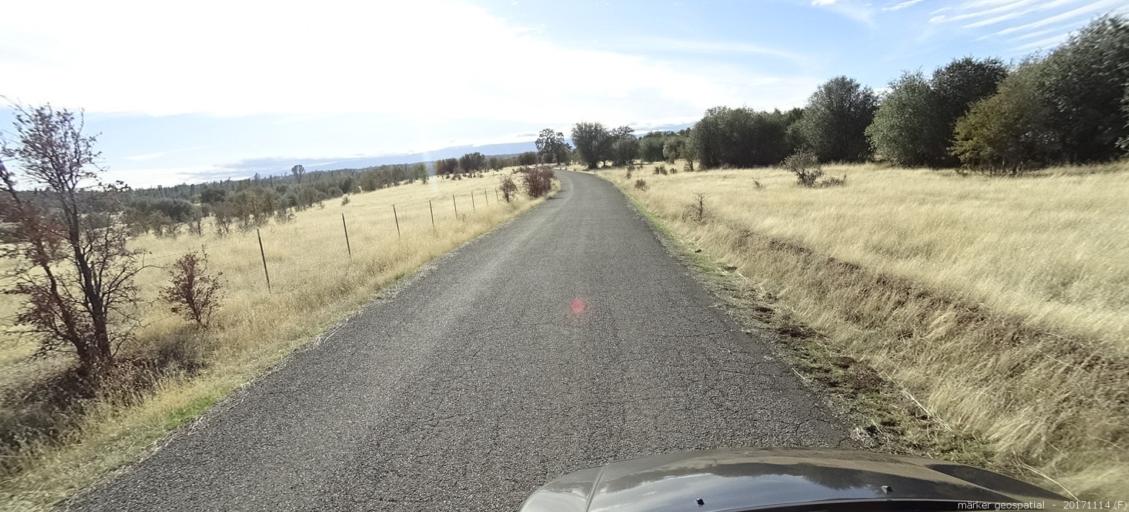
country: US
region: California
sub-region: Shasta County
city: Shasta
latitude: 40.3899
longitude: -122.5380
